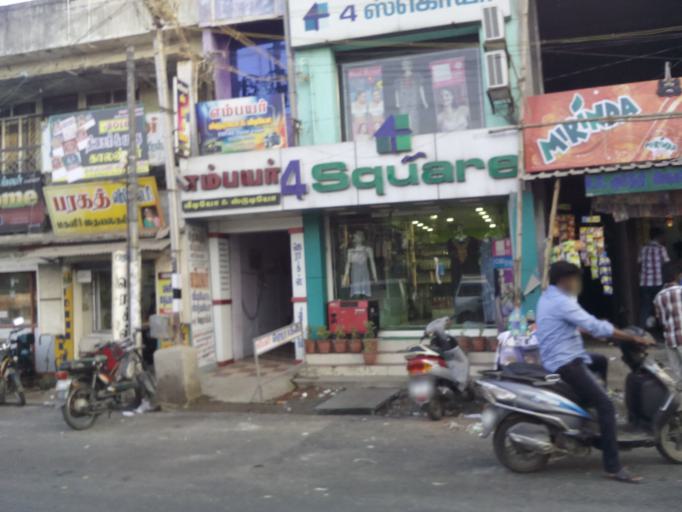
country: IN
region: Tamil Nadu
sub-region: Thanjavur
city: Kumbakonam
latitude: 10.9599
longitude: 79.3820
